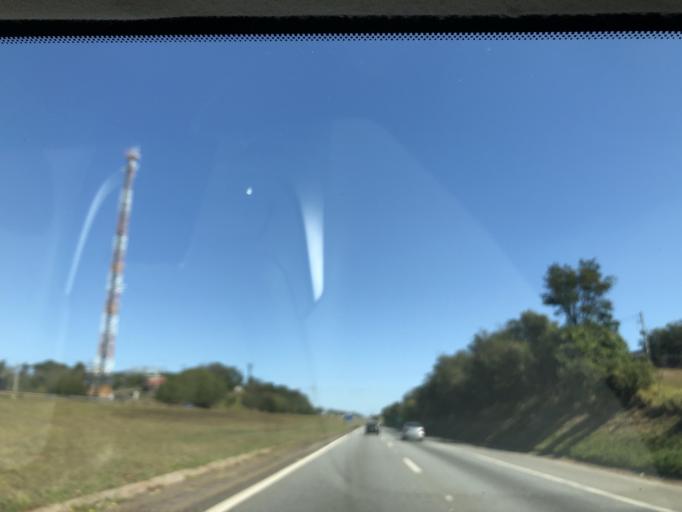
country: BR
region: Sao Paulo
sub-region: Sorocaba
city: Sorocaba
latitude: -23.4219
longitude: -47.3547
